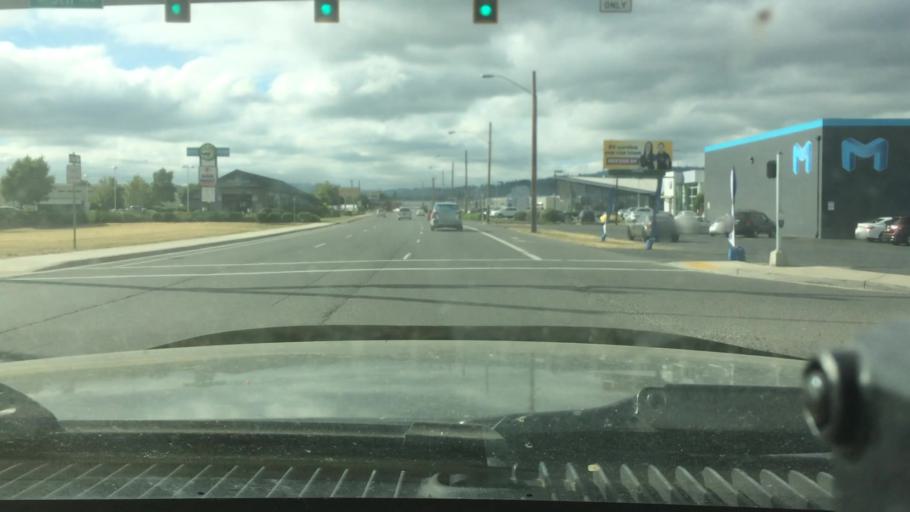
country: US
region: Oregon
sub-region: Lane County
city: Eugene
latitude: 44.0550
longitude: -123.1290
